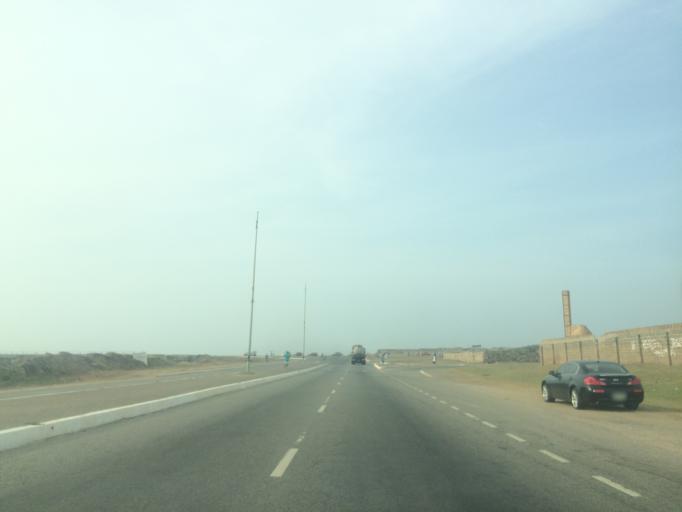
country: GH
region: Greater Accra
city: Accra
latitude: 5.5328
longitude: -0.2218
